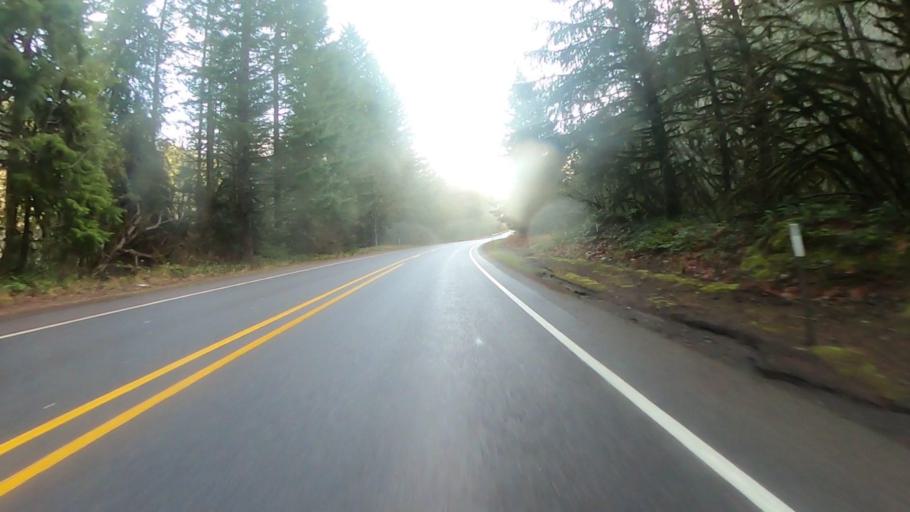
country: US
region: Oregon
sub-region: Lane County
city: Oakridge
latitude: 43.7202
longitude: -122.3343
